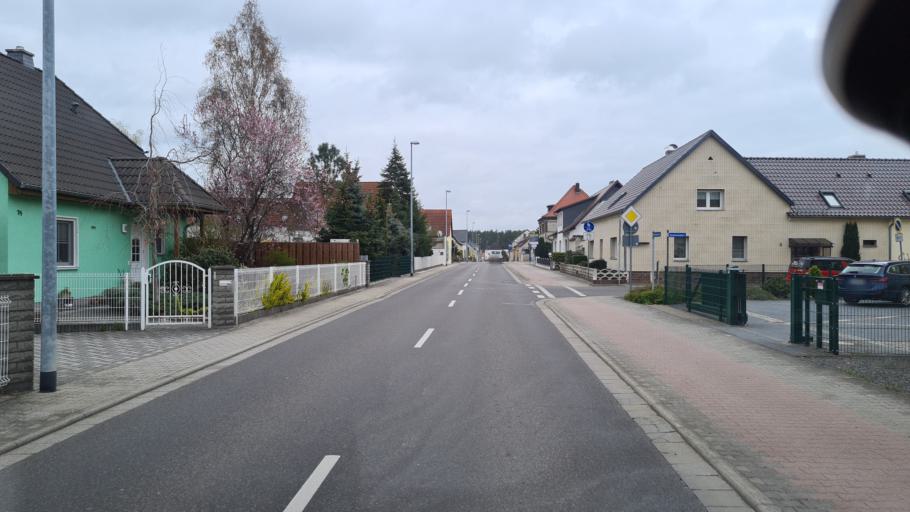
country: DE
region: Brandenburg
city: Schwarzheide
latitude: 51.4879
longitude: 13.8313
